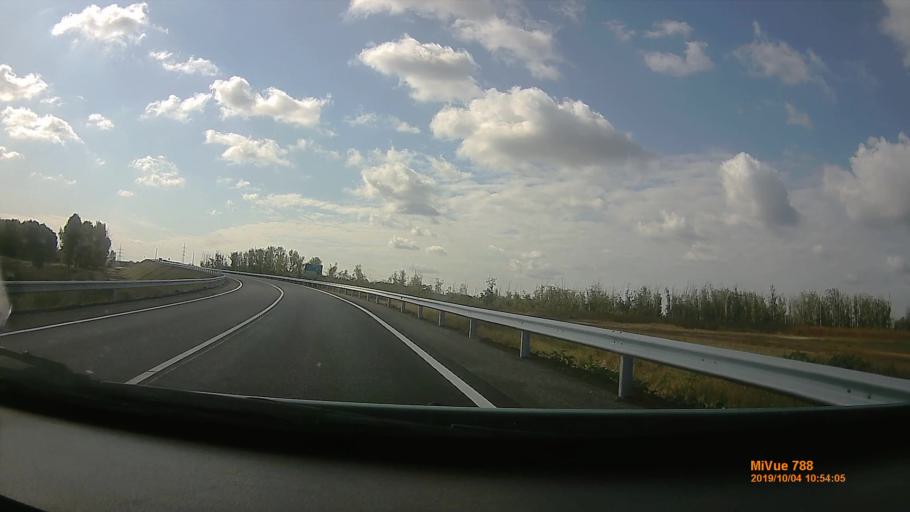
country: HU
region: Szabolcs-Szatmar-Bereg
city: Nyirtelek
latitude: 47.9840
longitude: 21.6657
